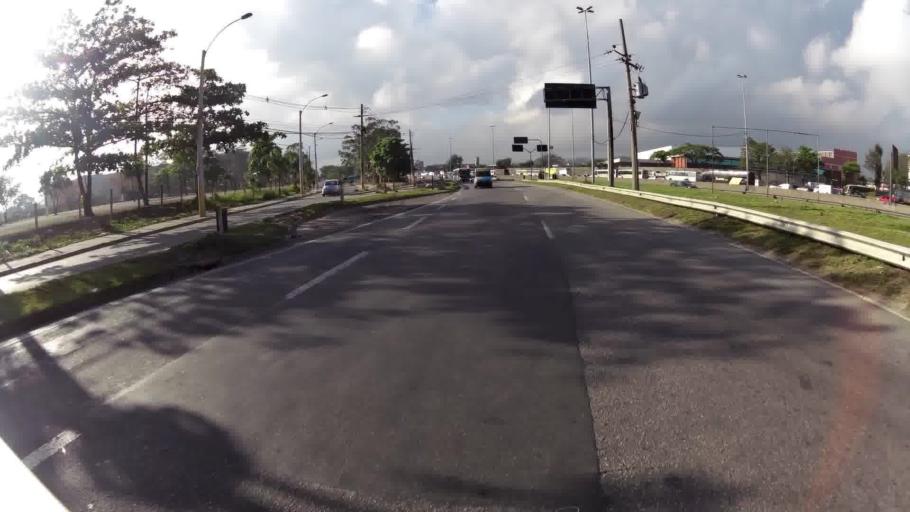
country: BR
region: Rio de Janeiro
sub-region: Duque De Caxias
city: Duque de Caxias
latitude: -22.8166
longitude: -43.2869
